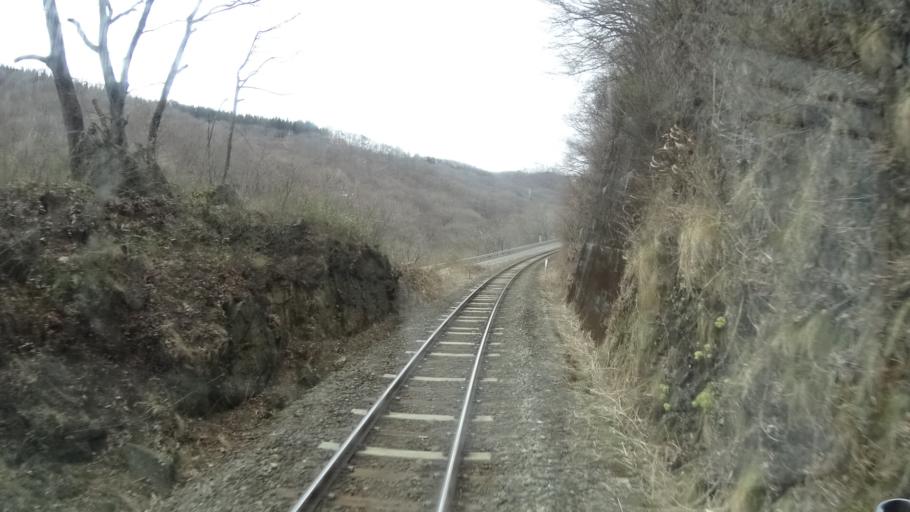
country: JP
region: Iwate
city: Hanamaki
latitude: 39.3612
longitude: 141.2930
